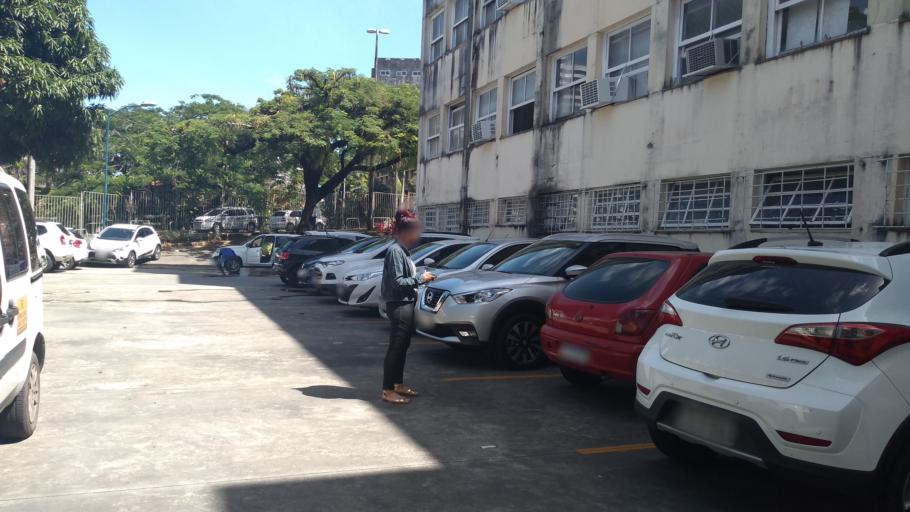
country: BR
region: Bahia
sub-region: Salvador
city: Salvador
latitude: -12.9941
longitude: -38.5215
